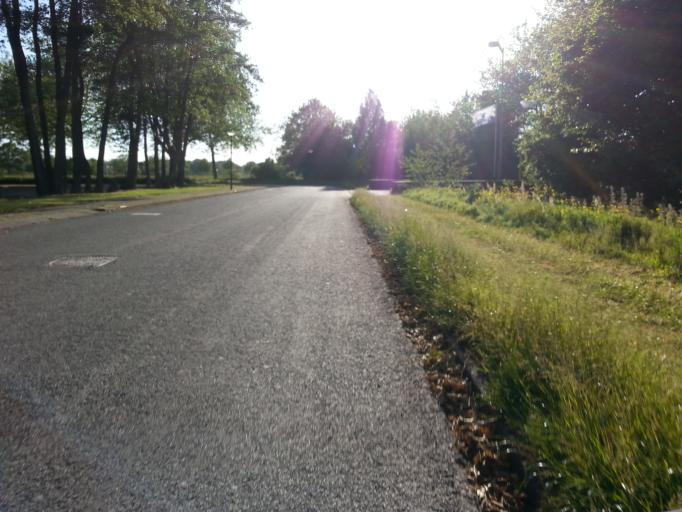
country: NL
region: Utrecht
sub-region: Gemeente Leusden
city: Leusden
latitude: 52.1412
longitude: 5.4236
